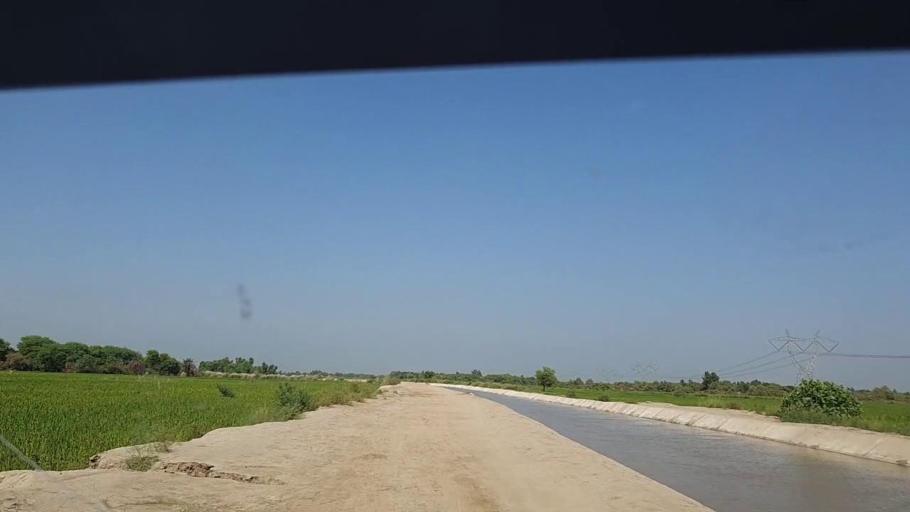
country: PK
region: Sindh
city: Ghauspur
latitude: 28.1601
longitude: 69.0924
